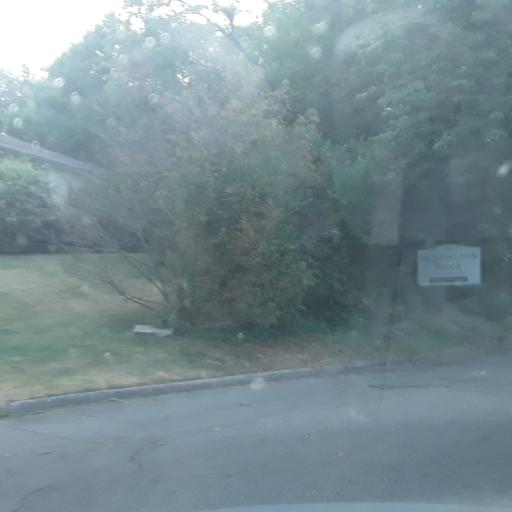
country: US
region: Tennessee
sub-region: Williamson County
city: Brentwood
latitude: 36.0519
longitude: -86.7319
